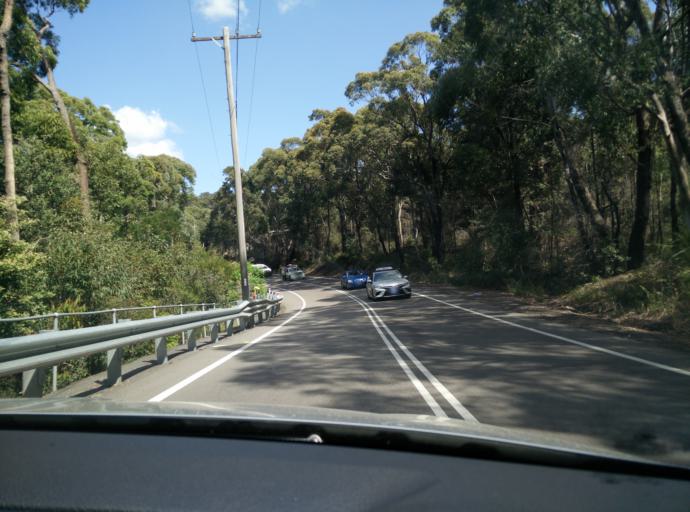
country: AU
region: New South Wales
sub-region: Gosford Shire
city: Blackwall
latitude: -33.4876
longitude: 151.3030
